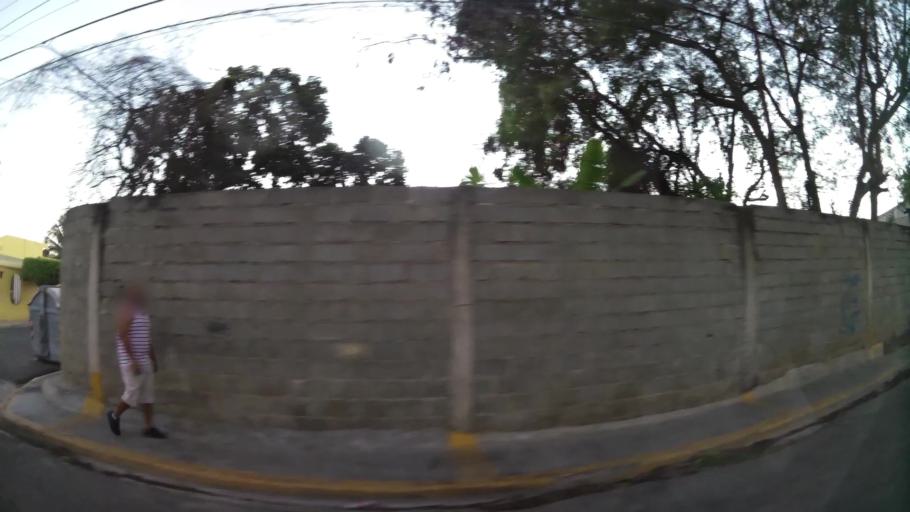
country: DO
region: Santo Domingo
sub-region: Santo Domingo
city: Santo Domingo Este
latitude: 18.4915
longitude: -69.8392
